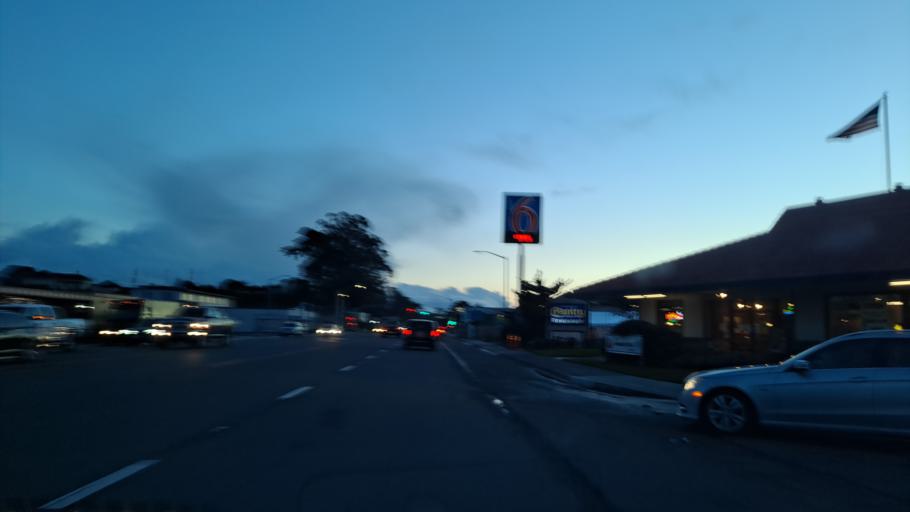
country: US
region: California
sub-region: Humboldt County
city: Bayview
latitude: 40.7907
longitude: -124.1790
